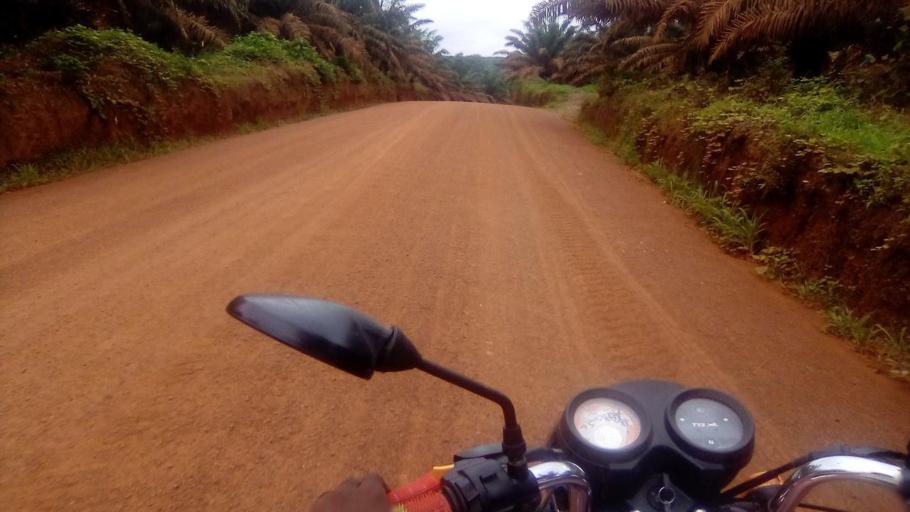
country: SL
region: Southern Province
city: Tongole
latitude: 7.4360
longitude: -11.8607
